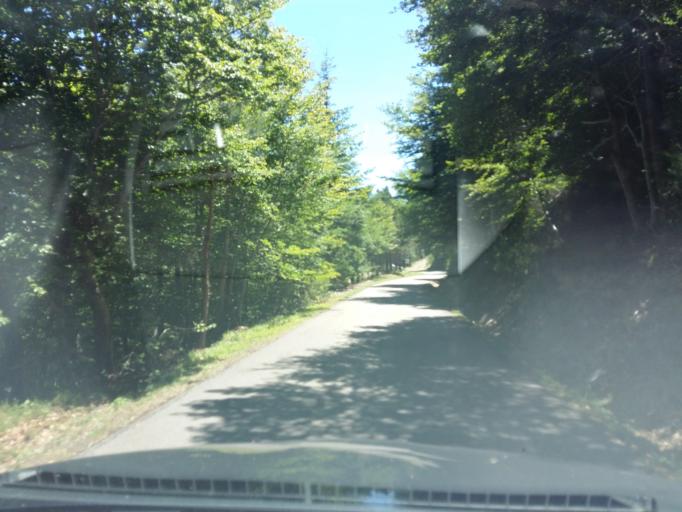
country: ES
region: Aragon
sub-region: Provincia de Zaragoza
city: Litago
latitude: 41.8004
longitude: -1.8078
